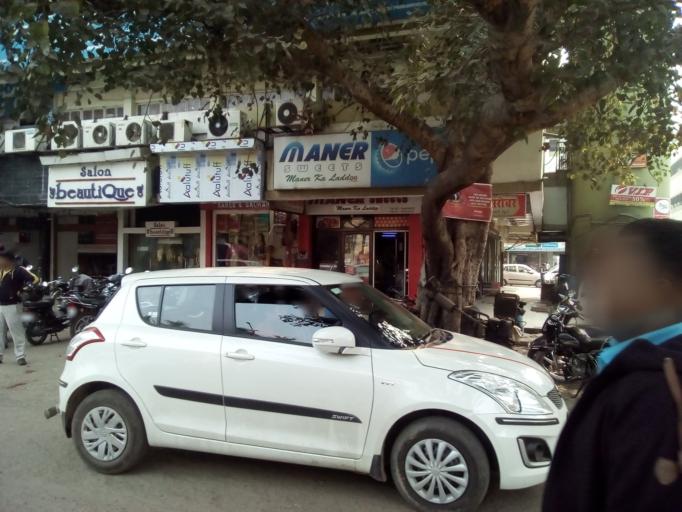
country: IN
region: Bihar
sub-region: Patna
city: Patna
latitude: 25.6103
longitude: 85.1341
